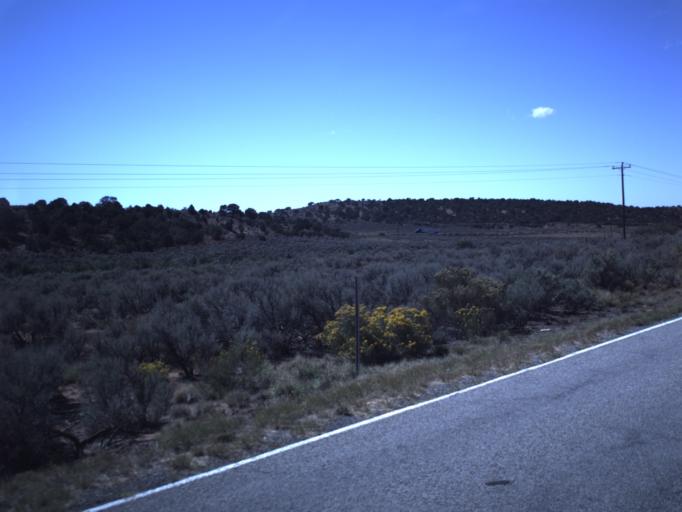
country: US
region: Utah
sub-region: Grand County
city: Moab
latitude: 38.3047
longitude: -109.3879
